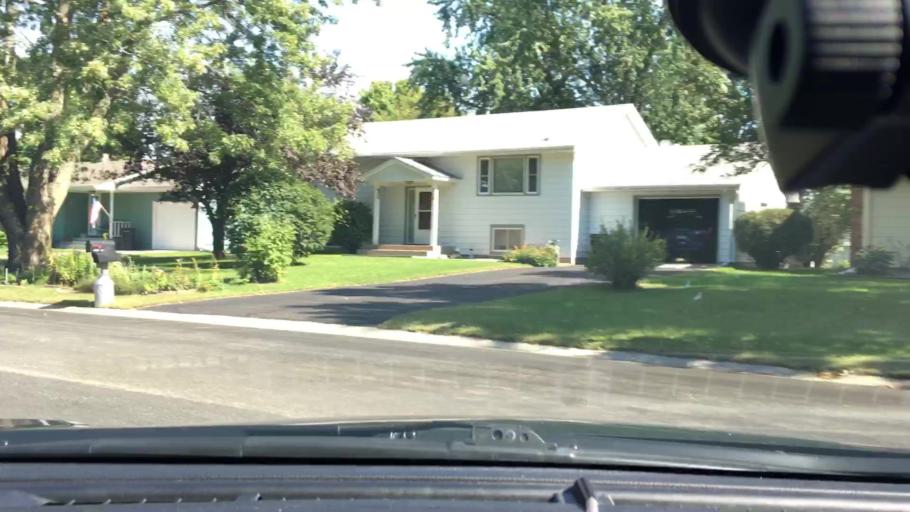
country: US
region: Minnesota
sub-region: Wright County
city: Saint Michael
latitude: 45.2024
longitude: -93.6663
